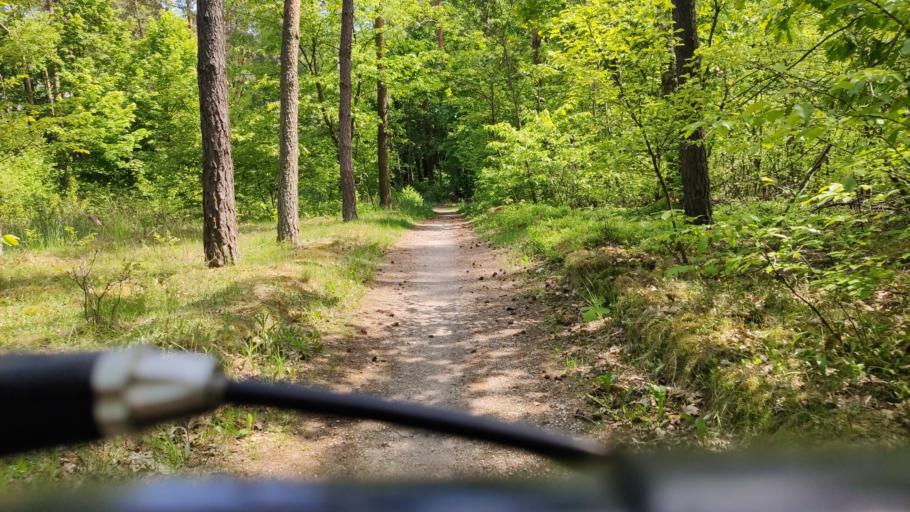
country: PL
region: Kujawsko-Pomorskie
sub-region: Wloclawek
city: Wloclawek
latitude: 52.6315
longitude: 19.1341
